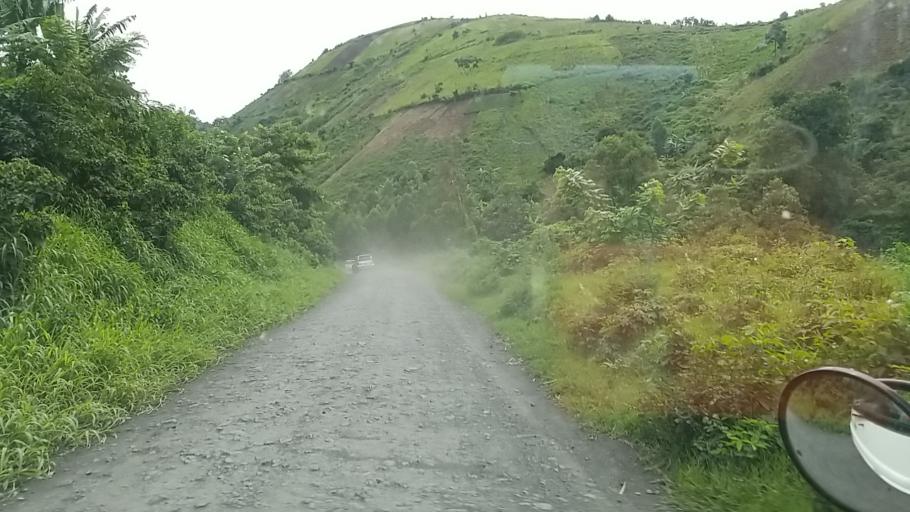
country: CD
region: Nord Kivu
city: Sake
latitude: -1.7429
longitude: 28.9937
